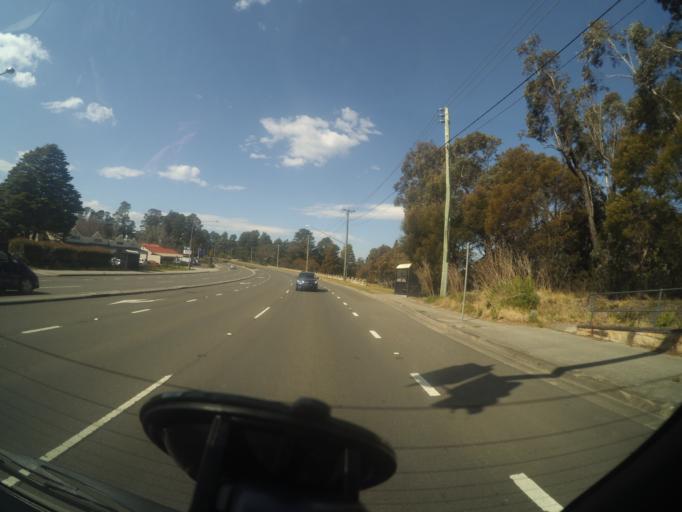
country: AU
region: New South Wales
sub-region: Blue Mountains Municipality
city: Leura
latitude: -33.7111
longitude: 150.3651
